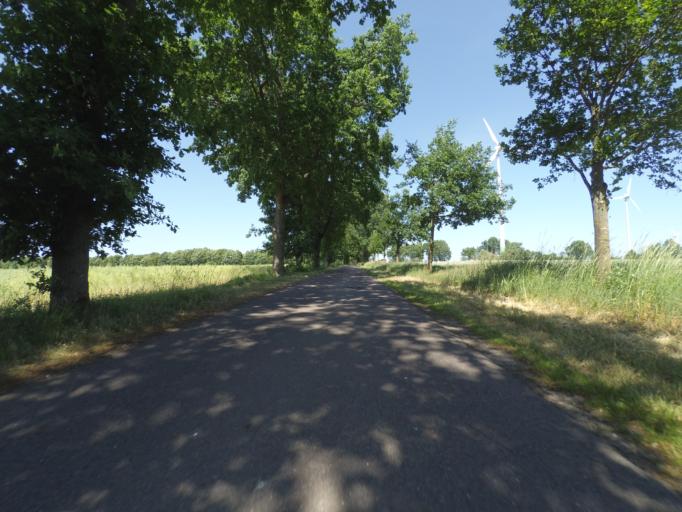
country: DE
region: Brandenburg
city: Gerdshagen
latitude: 53.2555
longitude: 12.2896
